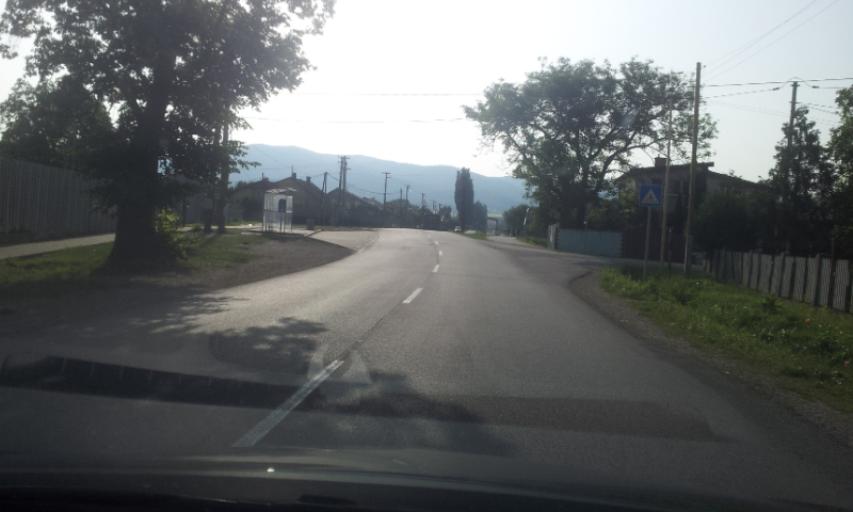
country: SK
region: Kosicky
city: Kosice
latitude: 48.6070
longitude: 21.3316
